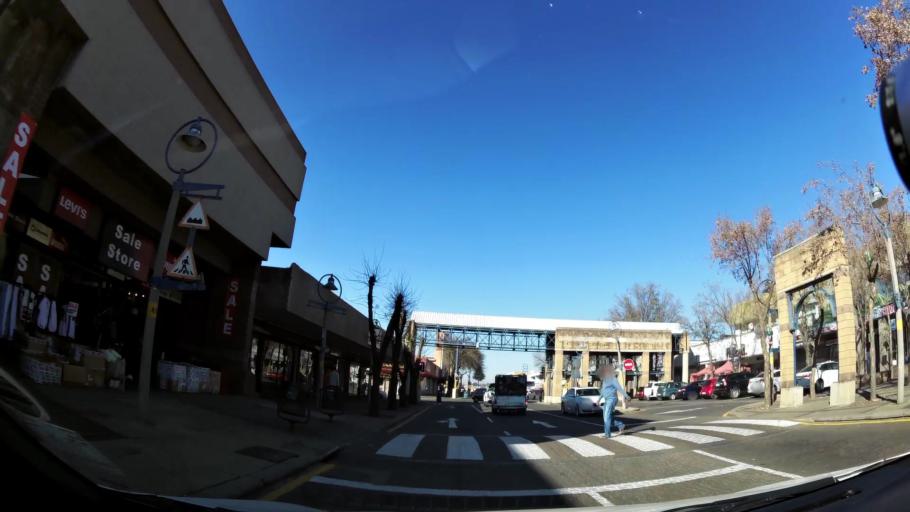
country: ZA
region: Gauteng
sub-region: Ekurhuleni Metropolitan Municipality
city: Germiston
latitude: -26.2665
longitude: 28.1222
